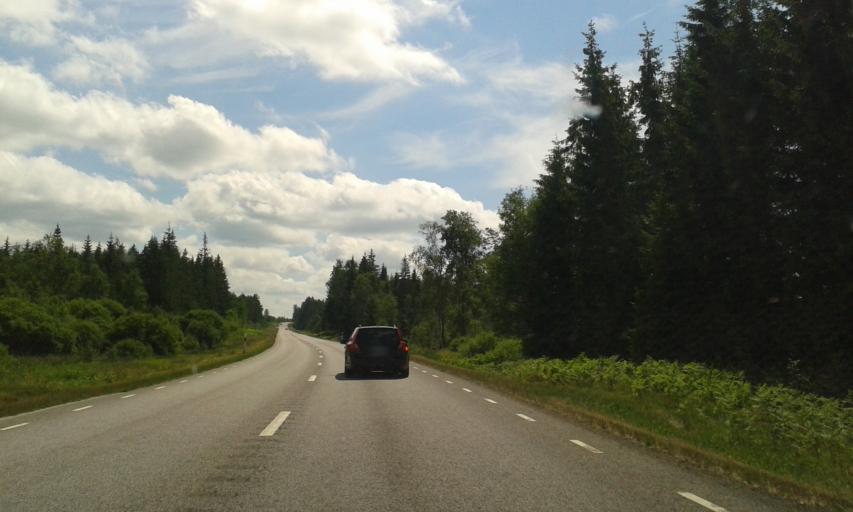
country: SE
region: Joenkoeping
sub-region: Varnamo Kommun
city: Rydaholm
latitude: 56.9632
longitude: 14.3404
